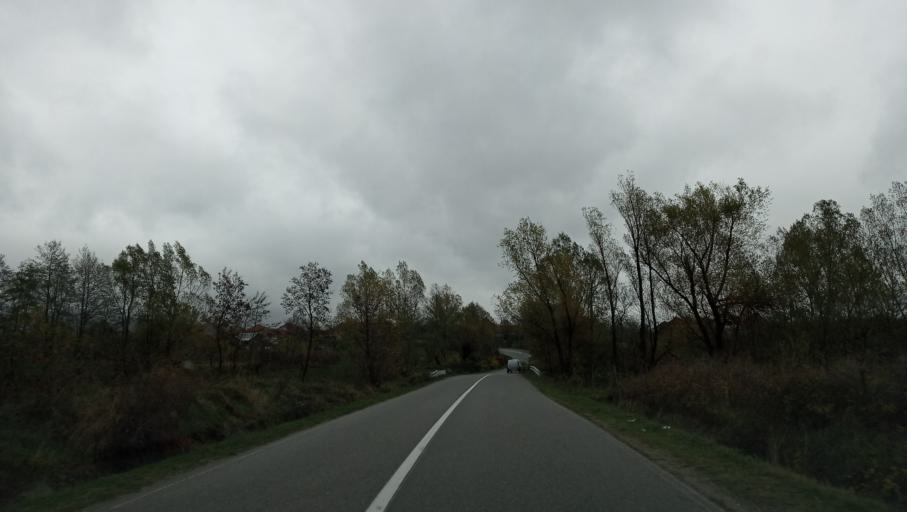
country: RO
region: Gorj
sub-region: Comuna Crasna
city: Crasna
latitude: 45.1664
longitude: 23.4801
